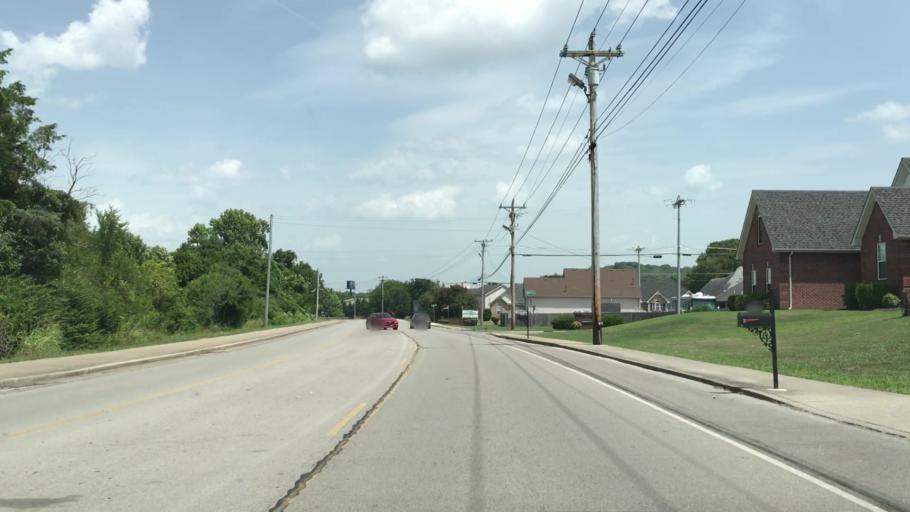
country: US
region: Tennessee
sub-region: Rutherford County
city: La Vergne
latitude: 35.9630
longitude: -86.5692
